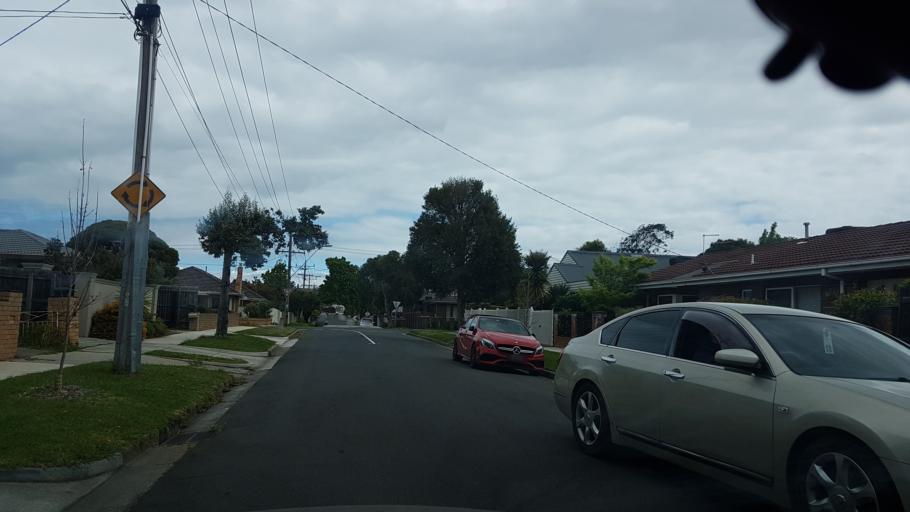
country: AU
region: Victoria
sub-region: Bayside
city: Moorabbin
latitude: -37.9319
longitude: 145.0426
